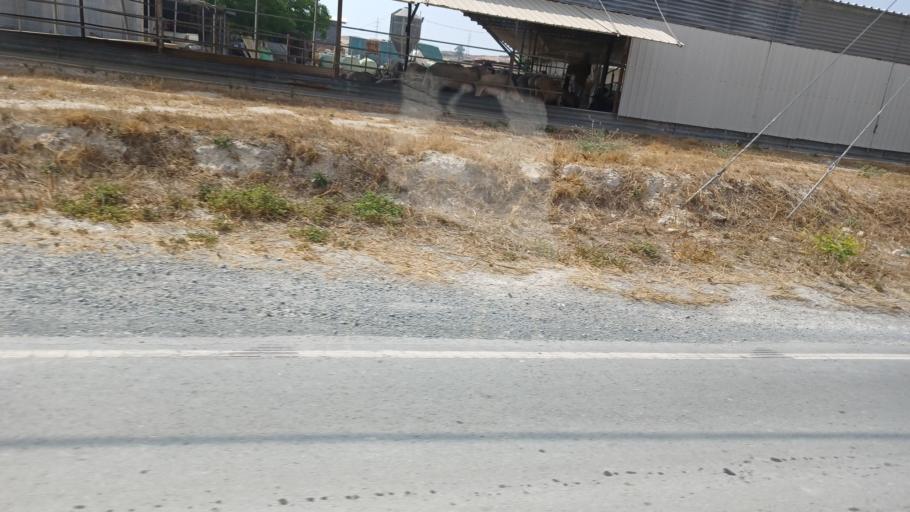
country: CY
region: Larnaka
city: Aradippou
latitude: 34.9357
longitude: 33.5482
